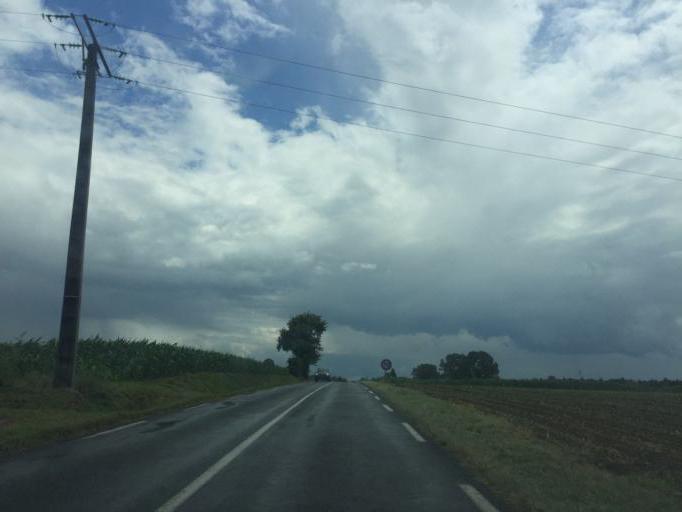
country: FR
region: Rhone-Alpes
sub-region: Departement du Rhone
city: Jons
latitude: 45.8002
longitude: 5.0938
